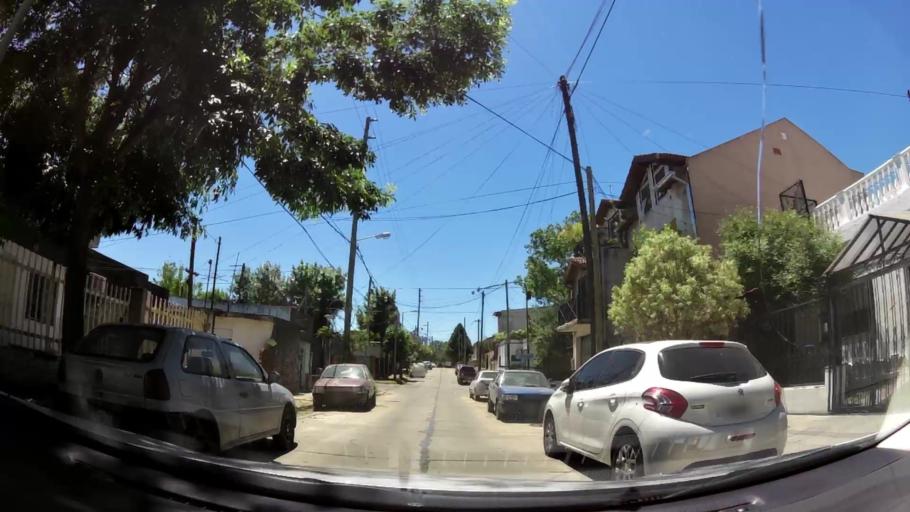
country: AR
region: Buenos Aires
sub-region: Partido de Tigre
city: Tigre
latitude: -34.4538
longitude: -58.5510
